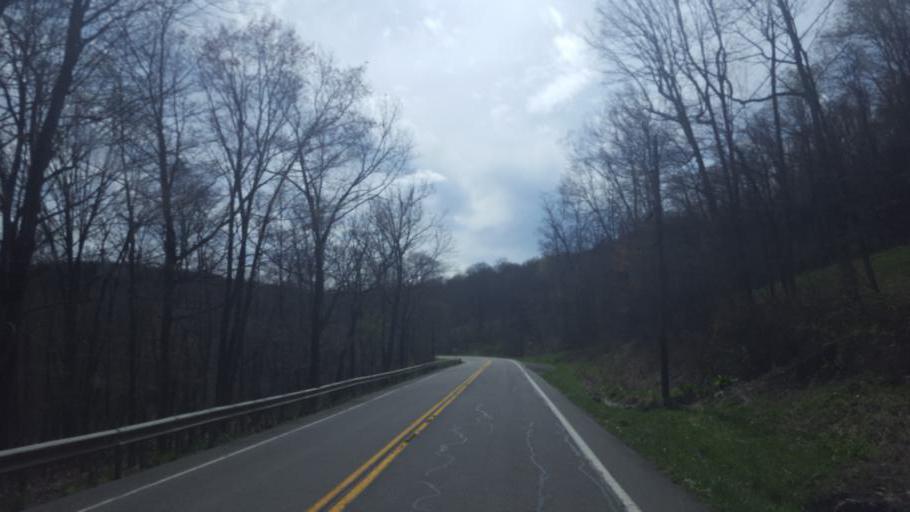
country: US
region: Pennsylvania
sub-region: Venango County
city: Sugarcreek
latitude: 41.3574
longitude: -79.9678
